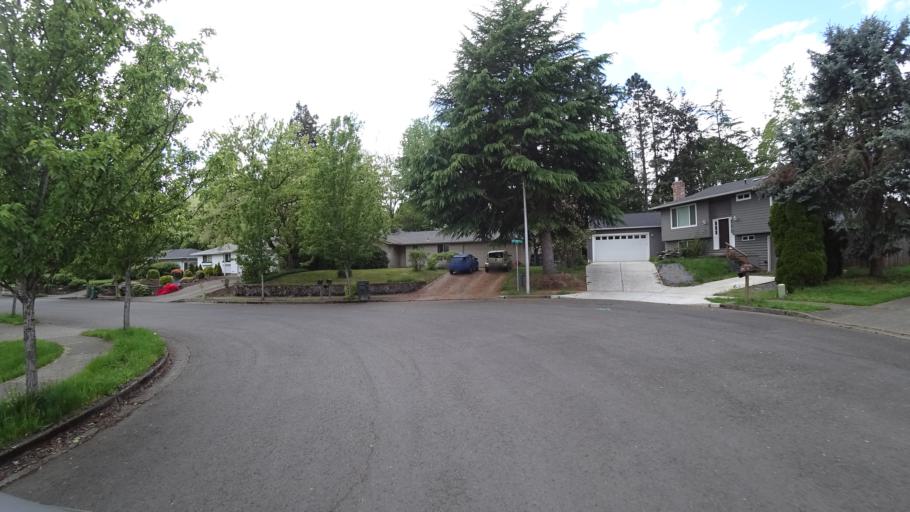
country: US
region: Oregon
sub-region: Washington County
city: Beaverton
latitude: 45.4806
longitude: -122.8233
